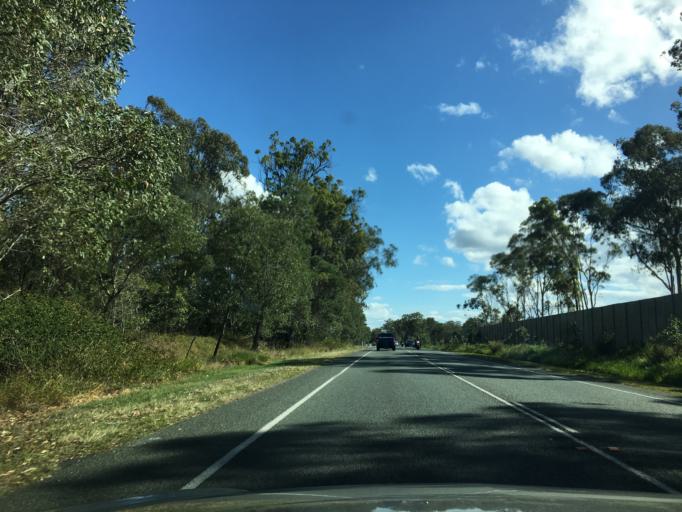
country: AU
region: Queensland
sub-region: Logan
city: Chambers Flat
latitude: -27.7753
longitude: 153.1033
